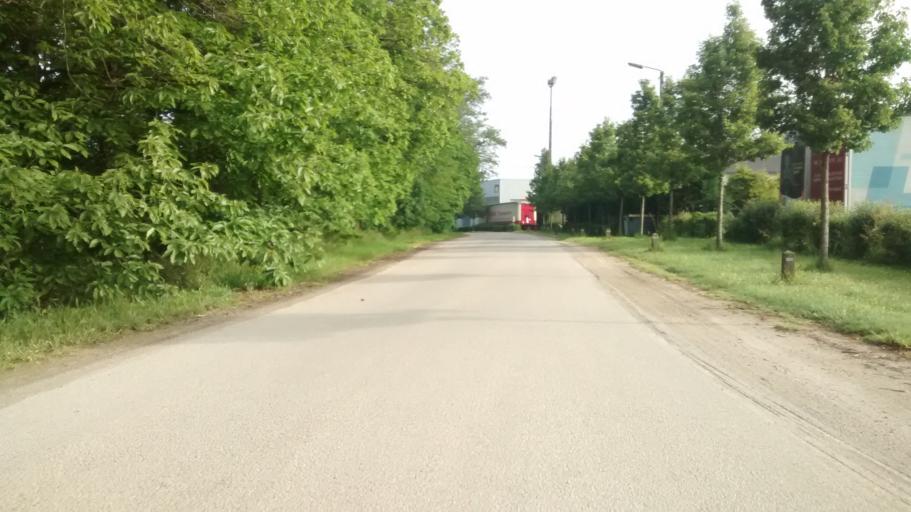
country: FR
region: Brittany
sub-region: Departement du Morbihan
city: Malestroit
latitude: 47.8006
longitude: -2.3997
